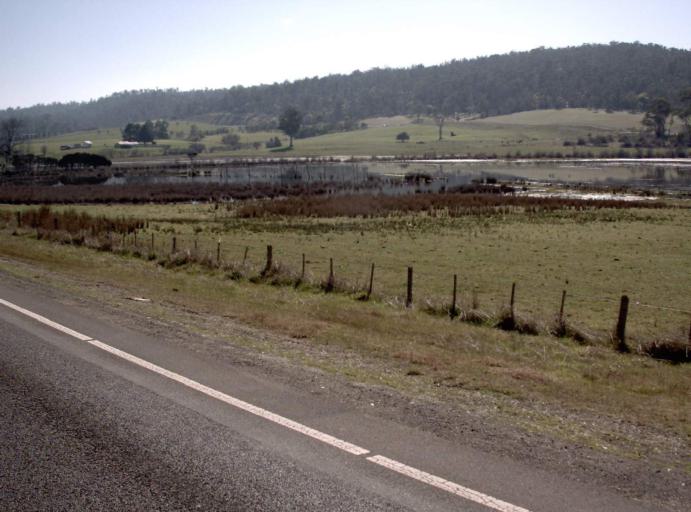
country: AU
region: Tasmania
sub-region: Launceston
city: Mayfield
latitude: -41.3198
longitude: 147.0591
